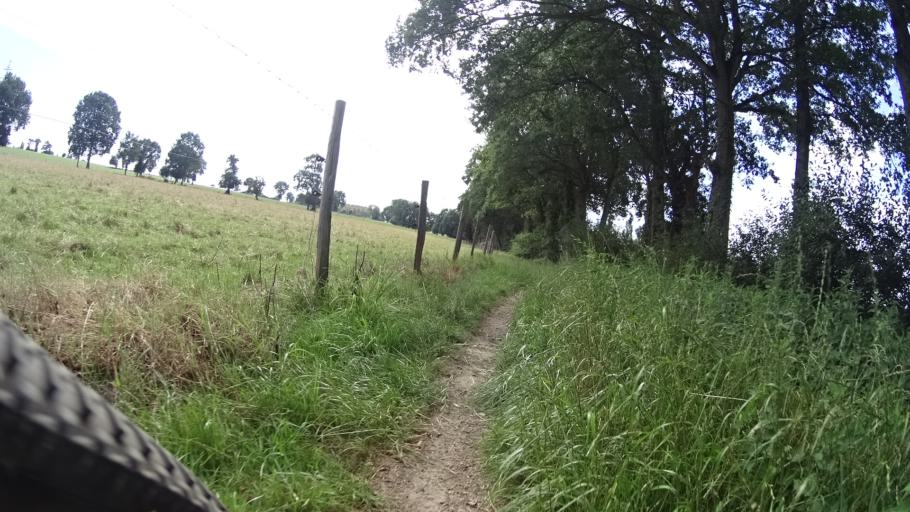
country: FR
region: Brittany
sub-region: Departement d'Ille-et-Vilaine
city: La Meziere
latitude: 48.2221
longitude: -1.7331
